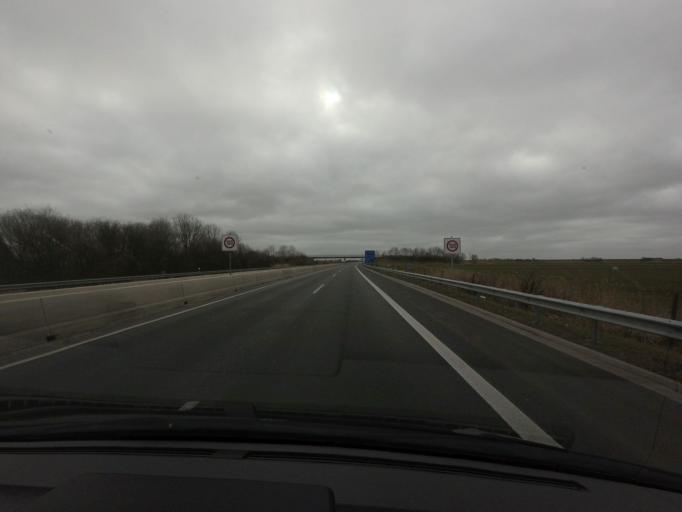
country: DE
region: Lower Saxony
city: Leer
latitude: 53.2446
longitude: 7.4223
